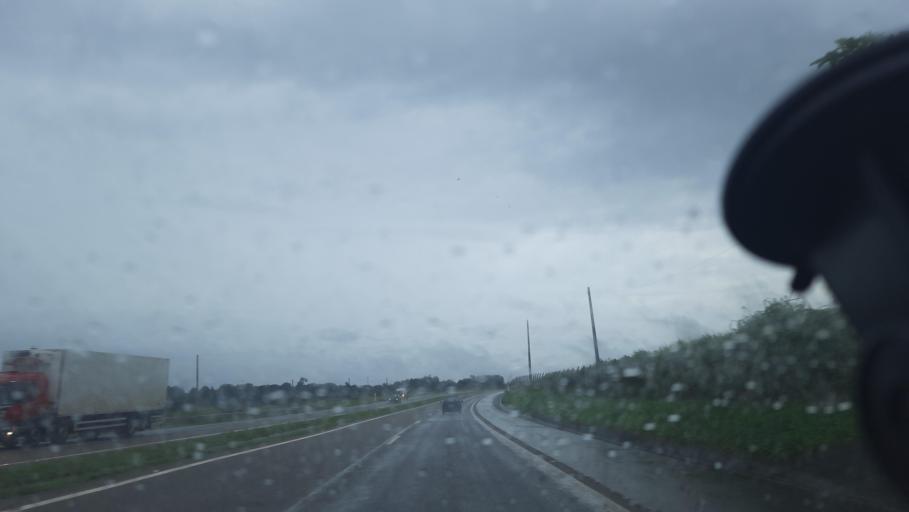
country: BR
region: Sao Paulo
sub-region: Casa Branca
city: Casa Branca
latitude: -21.8009
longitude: -47.0594
